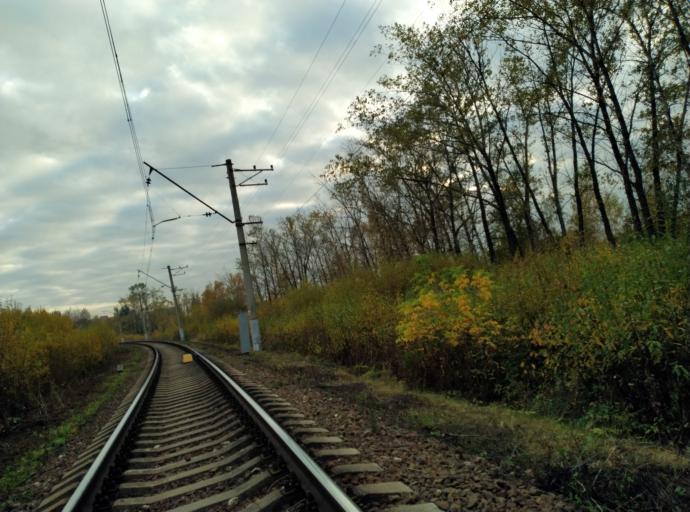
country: RU
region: Moskovskaya
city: Bol'shiye Vyazemy
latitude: 55.6344
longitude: 36.9761
